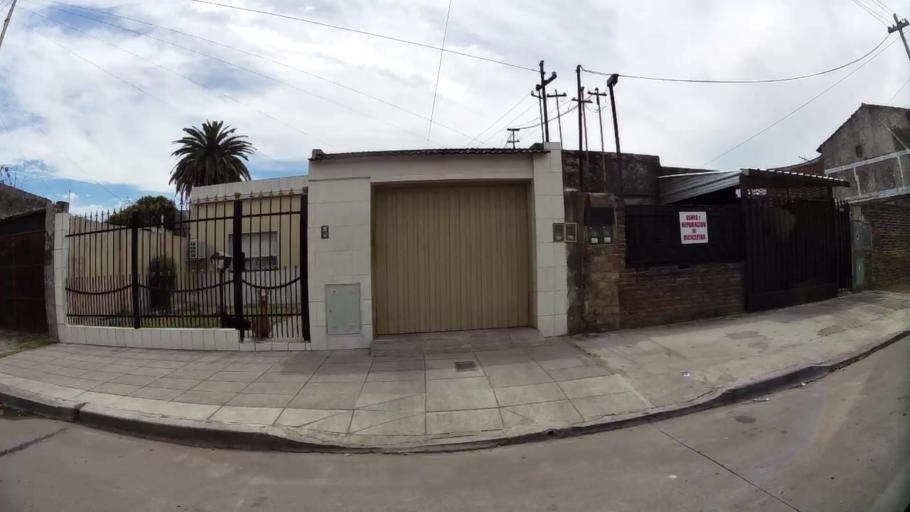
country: AR
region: Buenos Aires
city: San Justo
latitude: -34.6869
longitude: -58.5327
